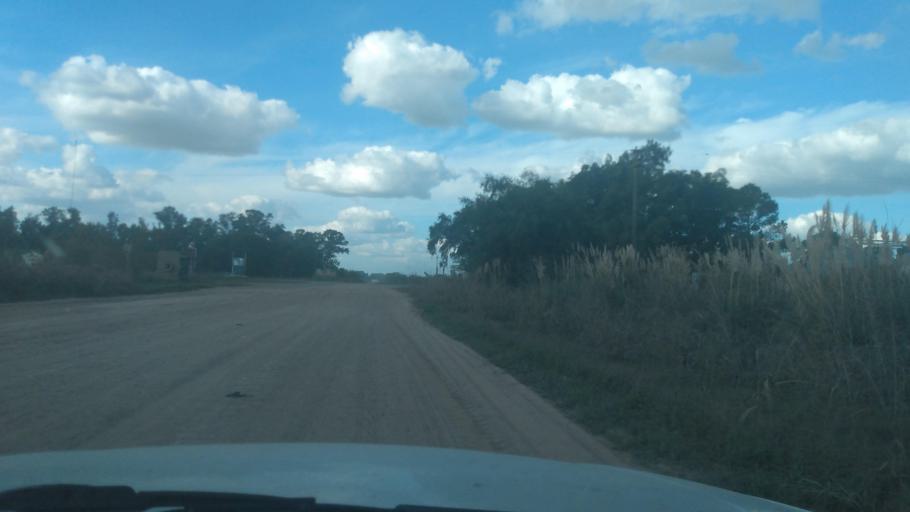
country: AR
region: Buenos Aires
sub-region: Partido de Navarro
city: Navarro
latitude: -34.9965
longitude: -59.3156
